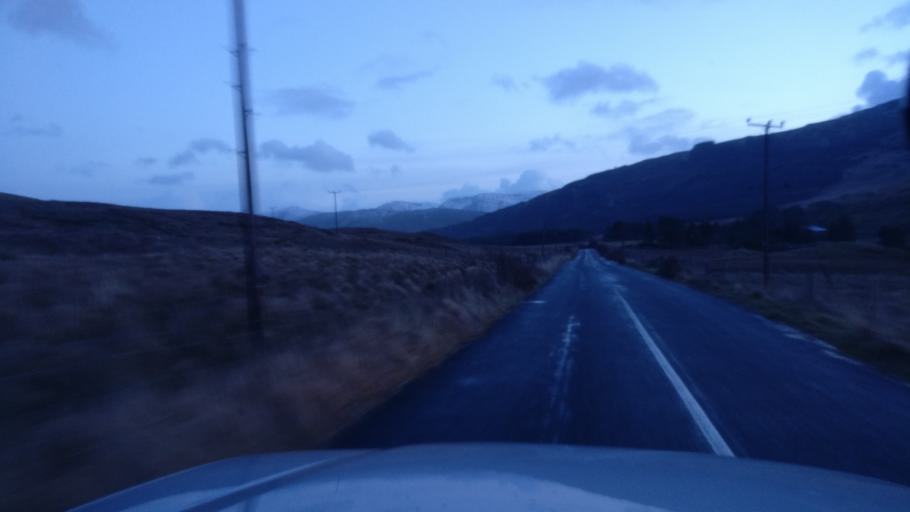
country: IE
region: Connaught
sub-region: Maigh Eo
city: Westport
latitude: 53.5625
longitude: -9.6487
